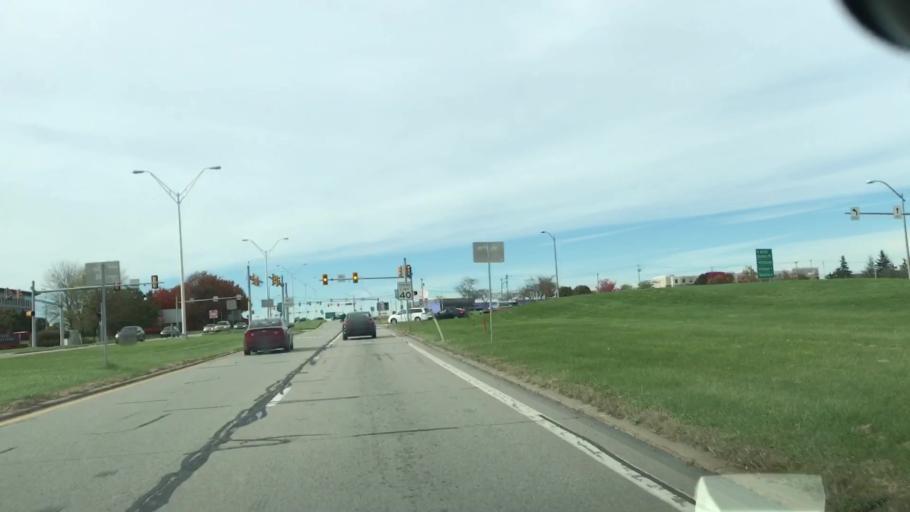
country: US
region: Pennsylvania
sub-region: Allegheny County
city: Carnot-Moon
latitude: 40.5001
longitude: -80.2182
